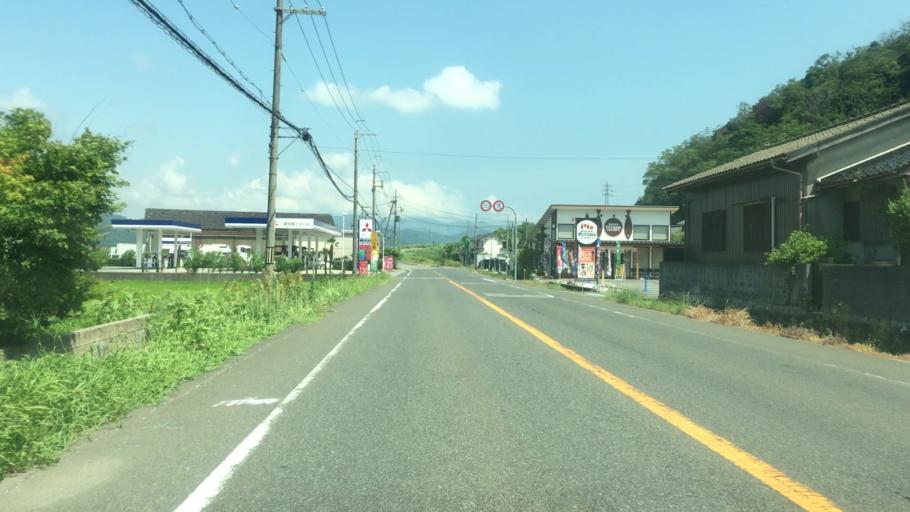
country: JP
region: Hyogo
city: Toyooka
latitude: 35.5650
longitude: 134.7924
